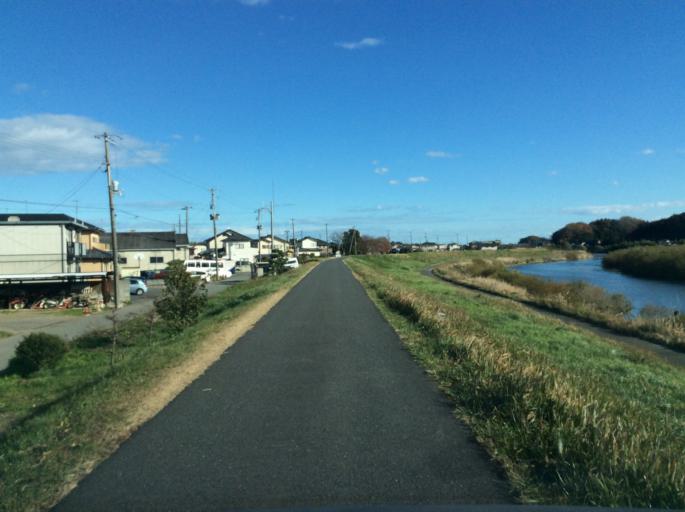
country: JP
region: Fukushima
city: Iwaki
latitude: 37.0602
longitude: 140.9285
